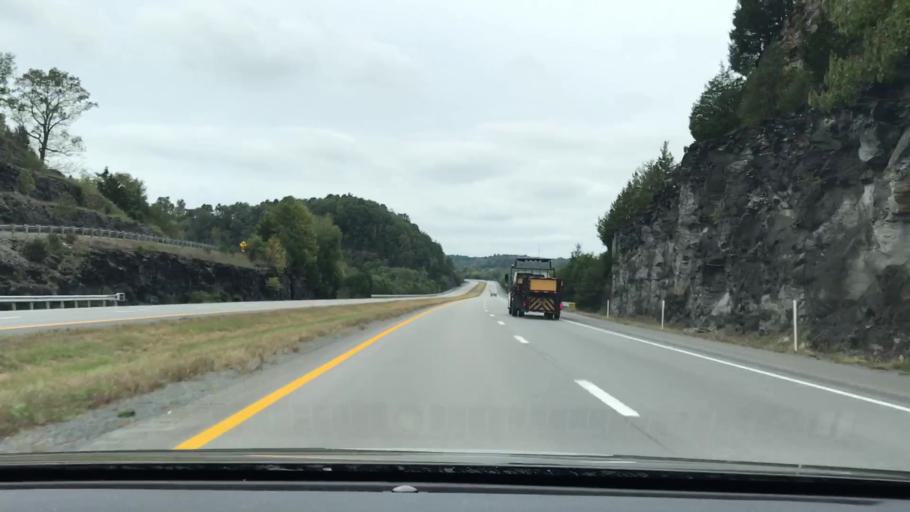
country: US
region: Kentucky
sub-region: Adair County
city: Columbia
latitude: 37.0570
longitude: -85.4288
